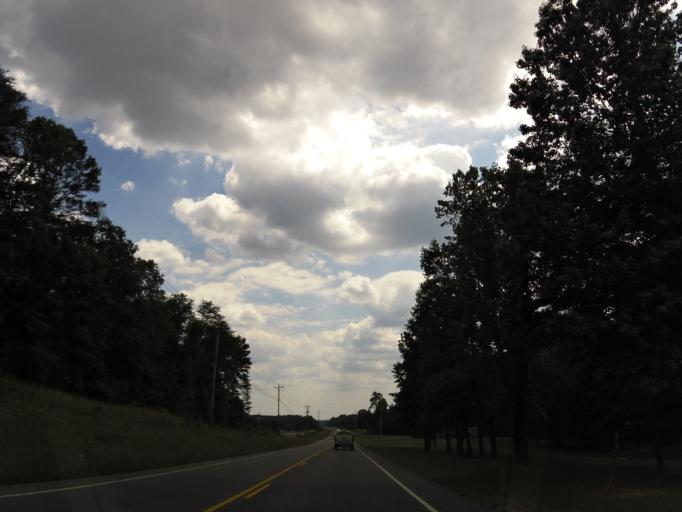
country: US
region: Tennessee
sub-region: Sequatchie County
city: Dunlap
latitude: 35.4175
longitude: -85.3619
